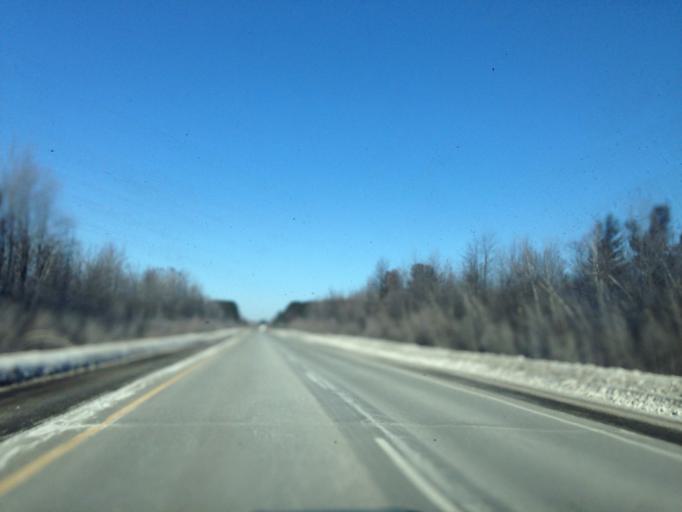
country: CA
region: Ontario
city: Ottawa
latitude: 45.3543
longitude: -75.4651
